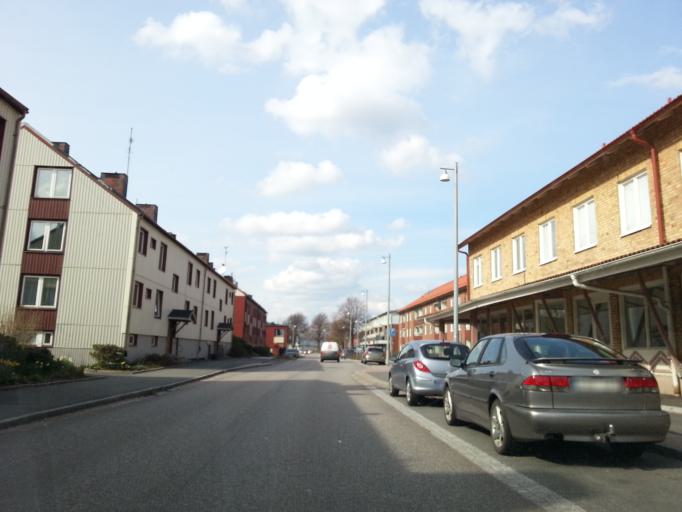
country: SE
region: Vaestra Goetaland
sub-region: Ale Kommun
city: Surte
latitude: 57.8267
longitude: 12.0154
